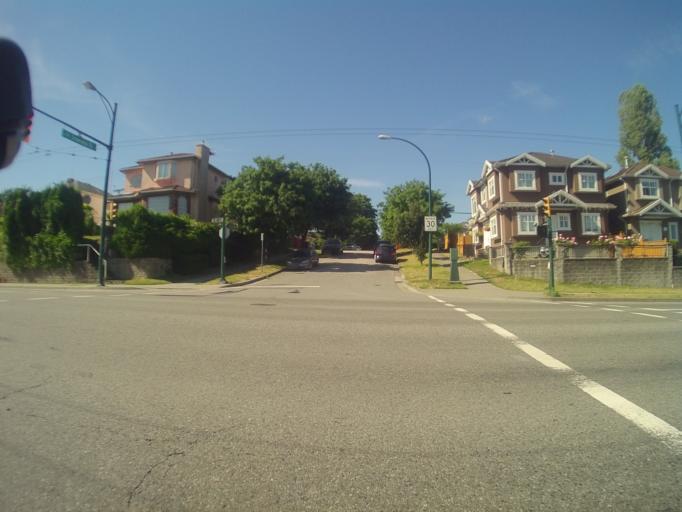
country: CA
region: British Columbia
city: Vancouver
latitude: 49.2327
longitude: -123.0797
